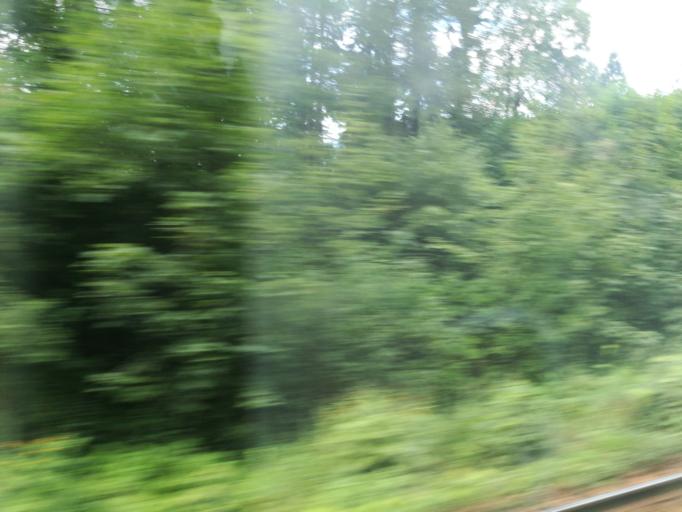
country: RO
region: Brasov
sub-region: Oras Predeal
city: Predeal
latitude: 45.5219
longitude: 25.5891
